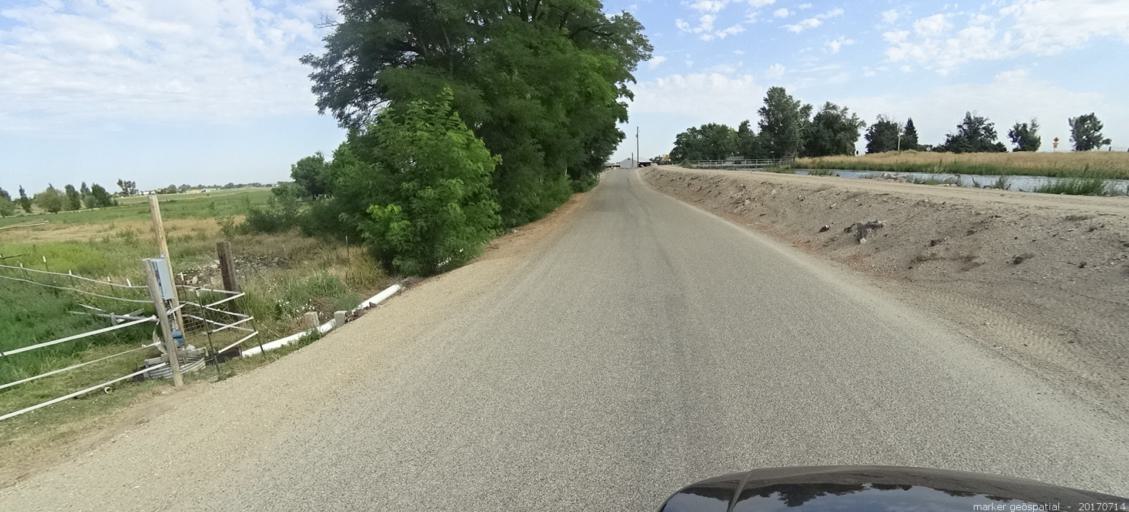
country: US
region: Idaho
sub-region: Ada County
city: Kuna
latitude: 43.4602
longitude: -116.3747
